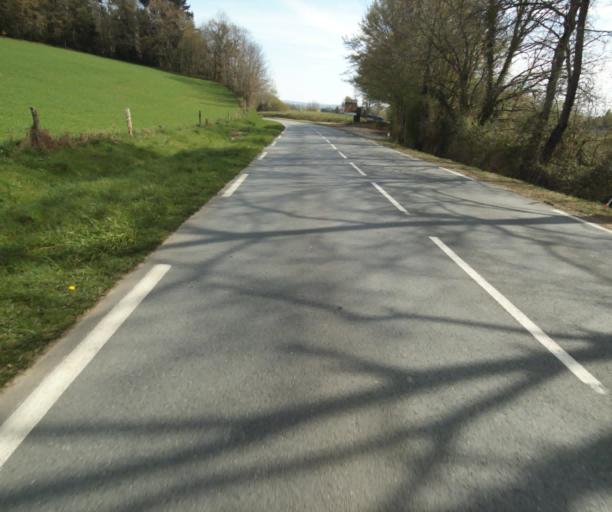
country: FR
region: Limousin
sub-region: Departement de la Correze
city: Naves
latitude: 45.3321
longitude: 1.7620
